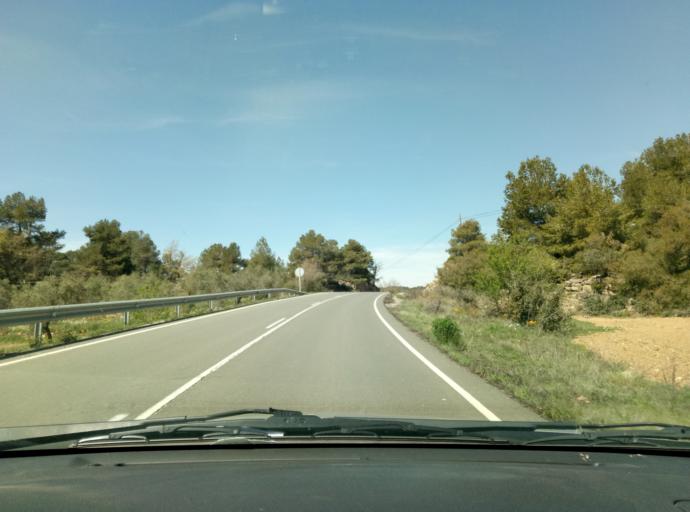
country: ES
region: Catalonia
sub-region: Provincia de Lleida
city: Vinaixa
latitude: 41.4237
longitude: 0.9134
